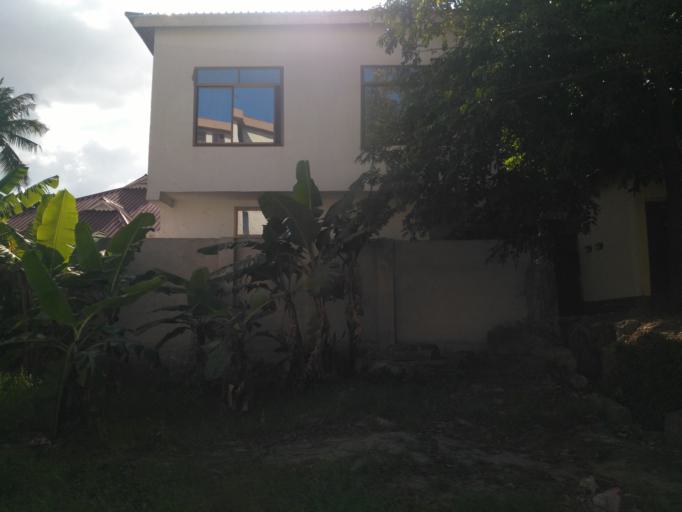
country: TZ
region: Dar es Salaam
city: Magomeni
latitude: -6.7812
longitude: 39.2664
